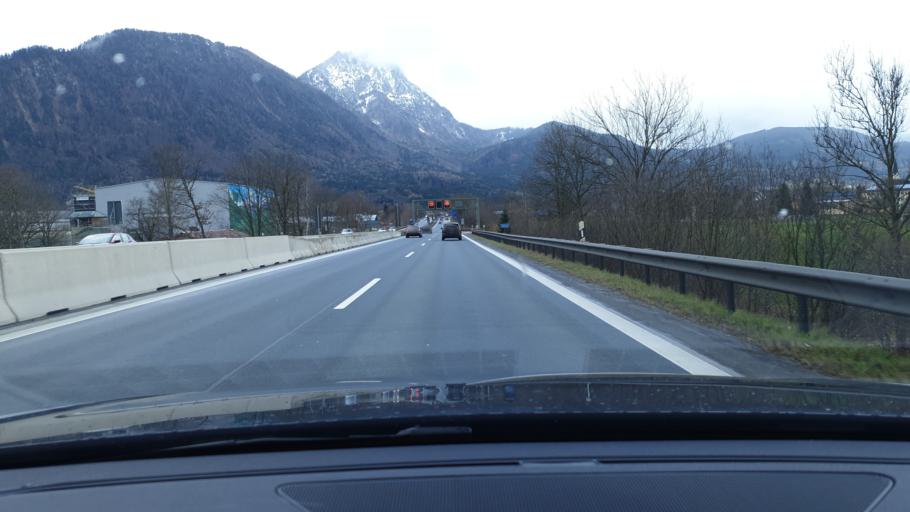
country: DE
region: Bavaria
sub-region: Upper Bavaria
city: Piding
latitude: 47.7655
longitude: 12.9229
